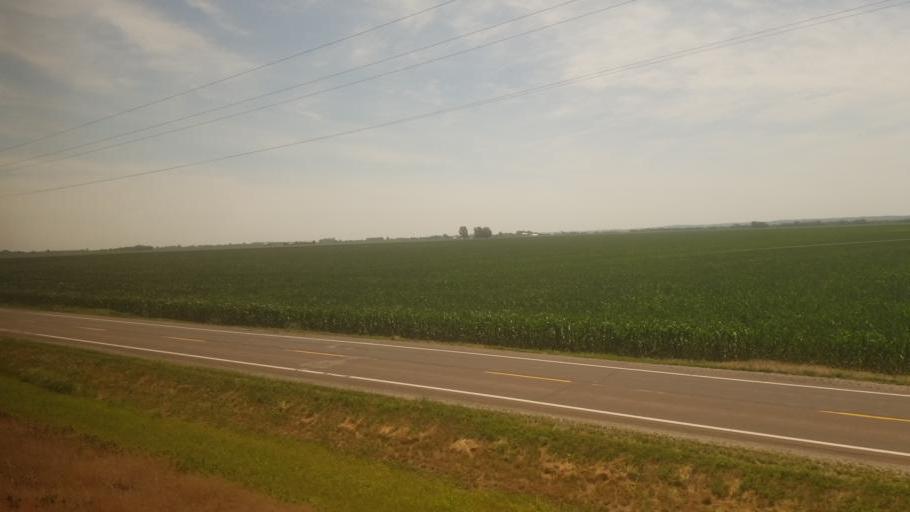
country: US
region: Missouri
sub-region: Carroll County
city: Carrollton
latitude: 39.3065
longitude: -93.6632
